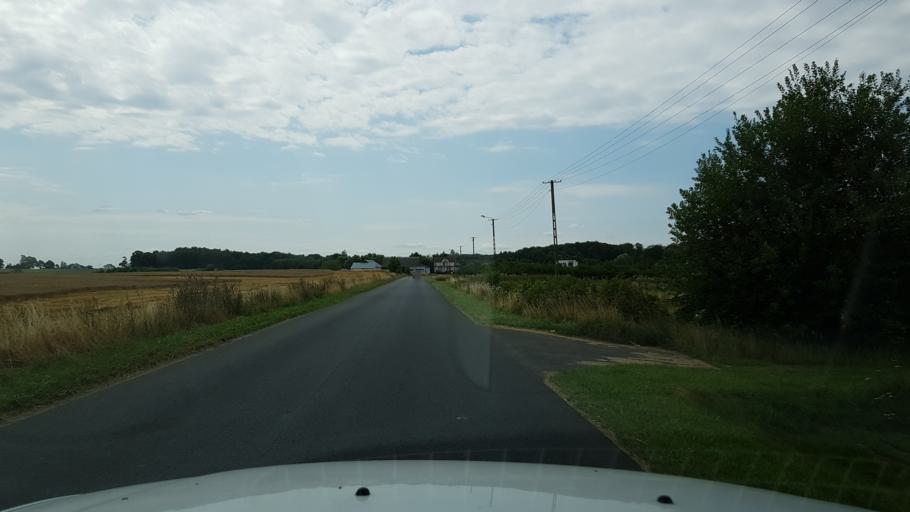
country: PL
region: West Pomeranian Voivodeship
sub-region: Powiat koszalinski
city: Mielno
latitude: 54.1766
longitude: 16.0096
